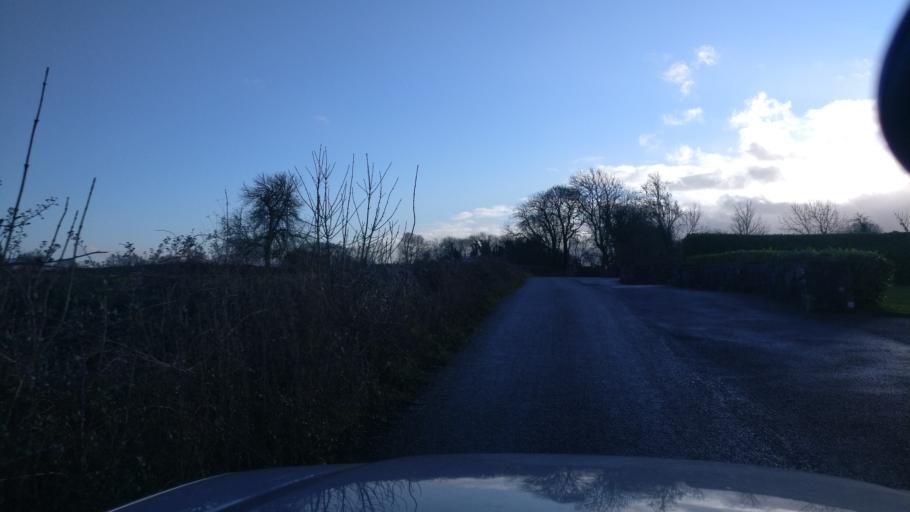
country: IE
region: Connaught
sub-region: County Galway
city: Loughrea
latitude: 53.2332
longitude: -8.5764
